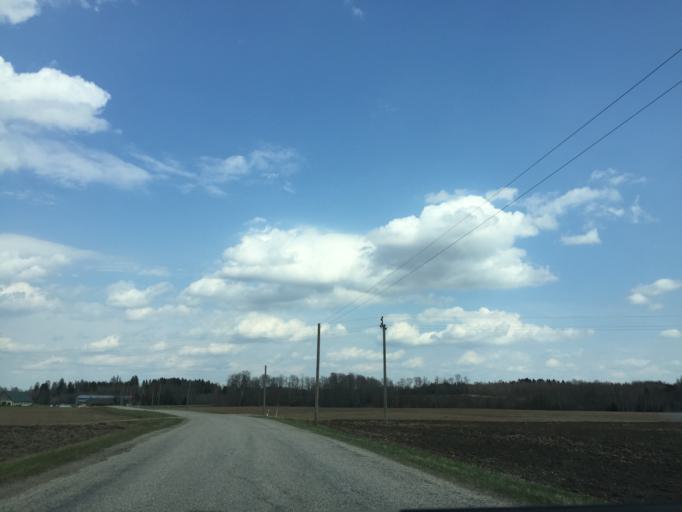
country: RU
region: Pskov
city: Pechory
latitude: 57.7170
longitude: 27.3251
